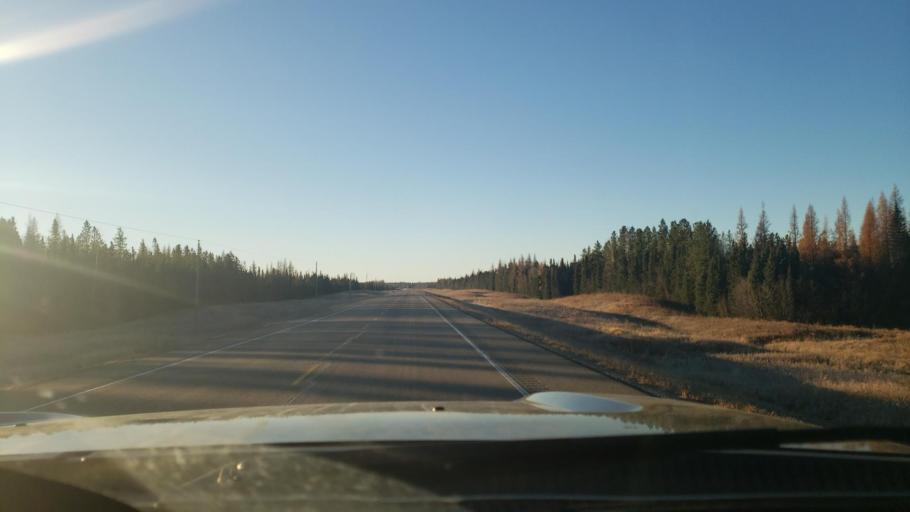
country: CA
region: British Columbia
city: Fort Nelson
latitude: 58.3706
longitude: -122.7136
